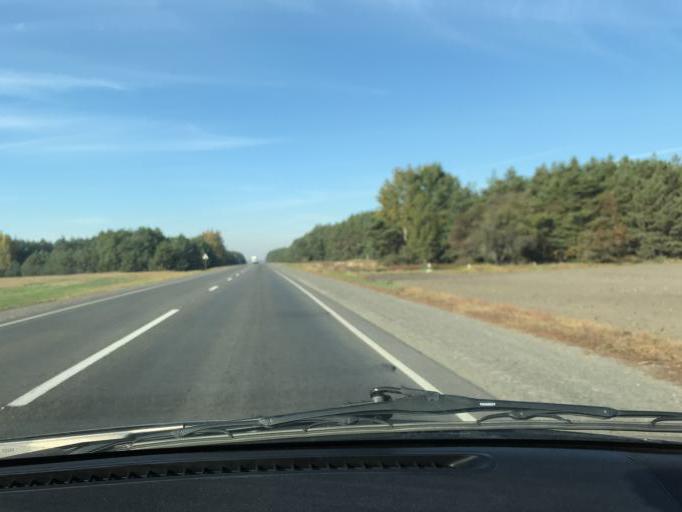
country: BY
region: Brest
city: Davyd-Haradok
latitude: 52.2378
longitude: 27.2227
